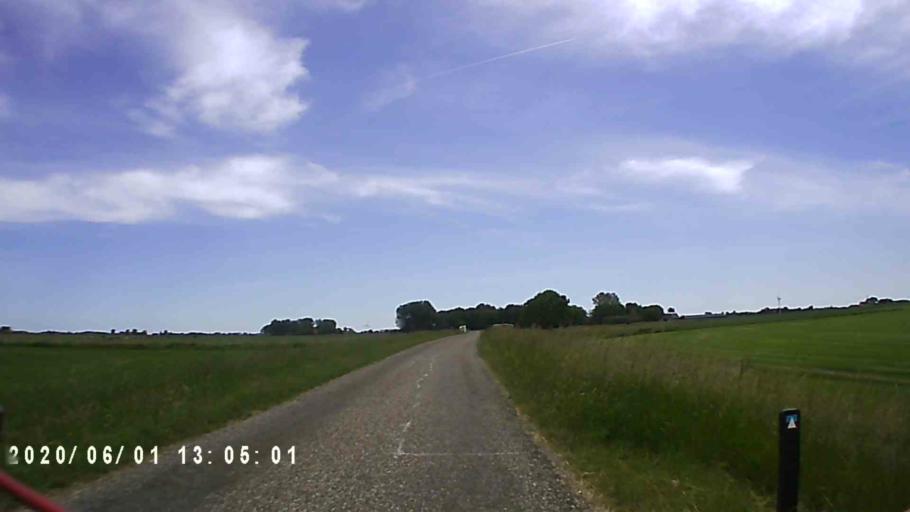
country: NL
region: Friesland
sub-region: Gemeente Franekeradeel
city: Tzum
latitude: 53.1378
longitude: 5.5462
